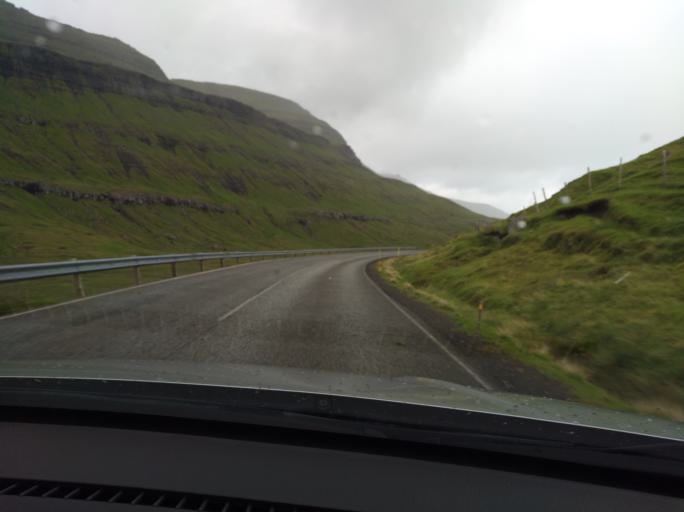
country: FO
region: Eysturoy
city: Fuglafjordur
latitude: 62.2319
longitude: -6.8804
